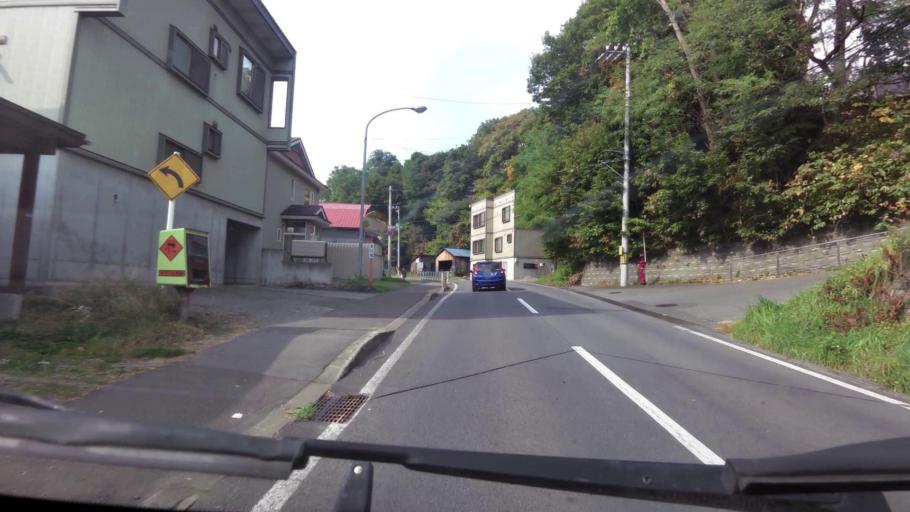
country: JP
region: Hokkaido
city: Otaru
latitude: 43.1421
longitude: 141.1560
